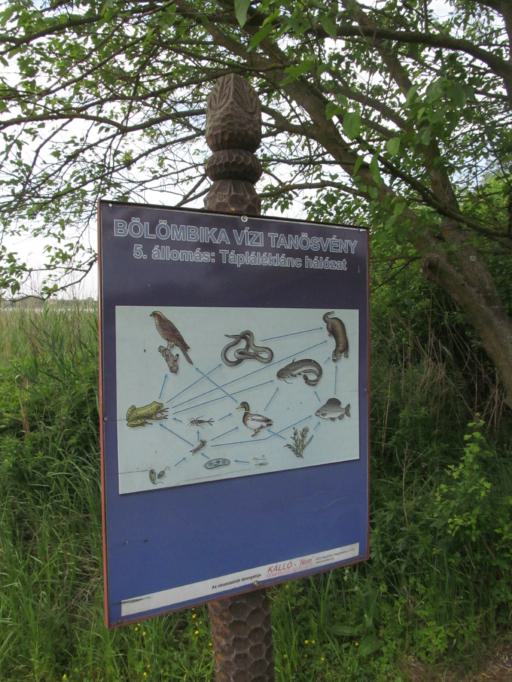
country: HU
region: Szabolcs-Szatmar-Bereg
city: Nagykallo
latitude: 47.8951
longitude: 21.8509
